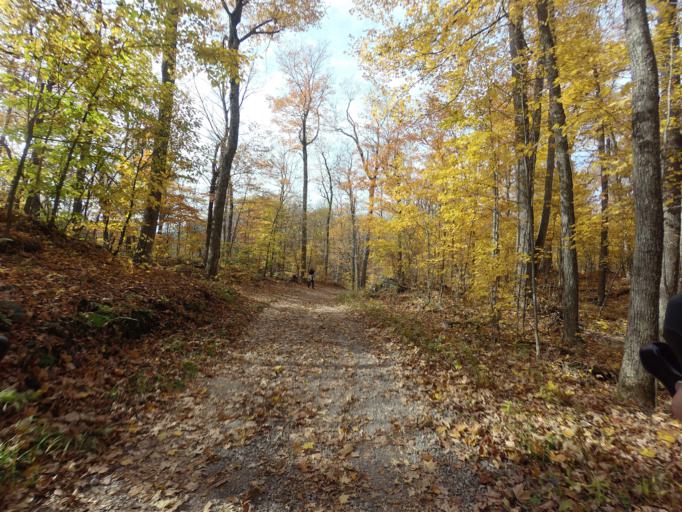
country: CA
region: Quebec
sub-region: Outaouais
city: Wakefield
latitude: 45.5025
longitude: -75.8692
